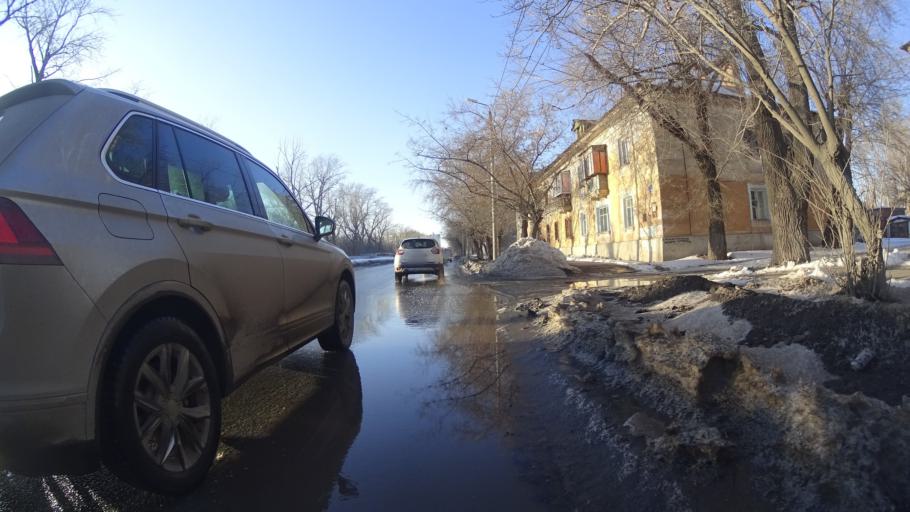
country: RU
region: Chelyabinsk
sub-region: Gorod Chelyabinsk
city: Chelyabinsk
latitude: 55.1328
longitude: 61.4614
